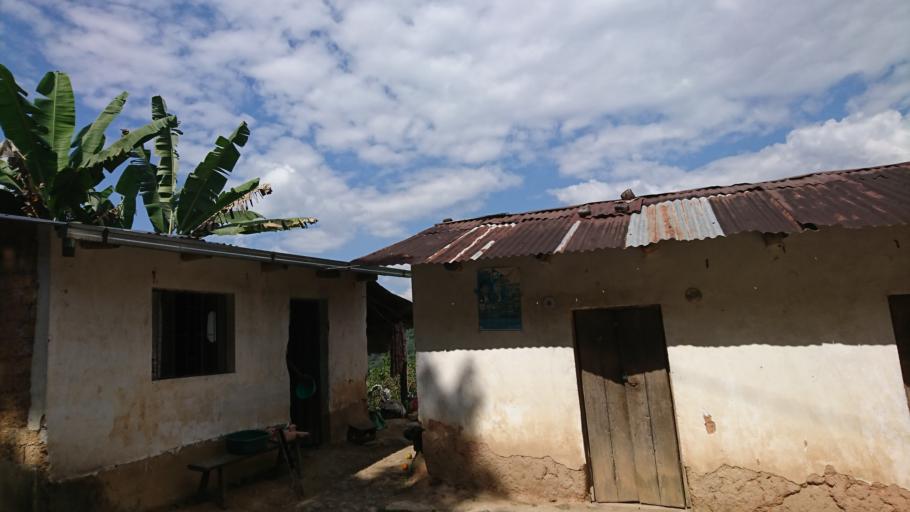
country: BO
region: La Paz
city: Coroico
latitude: -16.0763
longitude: -67.7882
